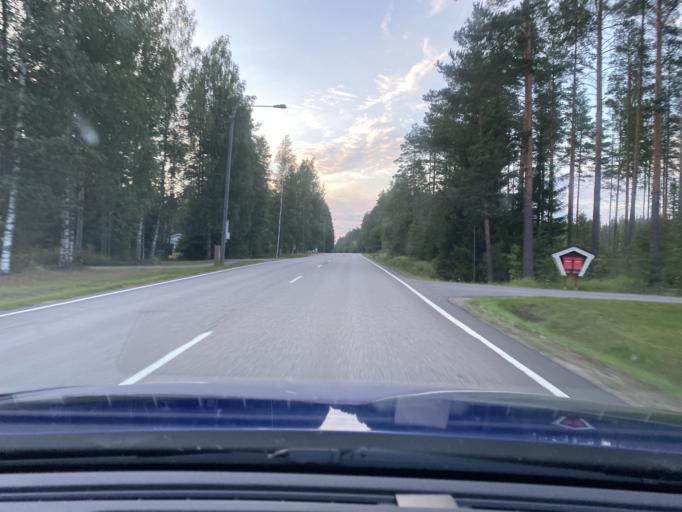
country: FI
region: Satakunta
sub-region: Pohjois-Satakunta
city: Honkajoki
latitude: 61.9544
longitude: 22.2250
